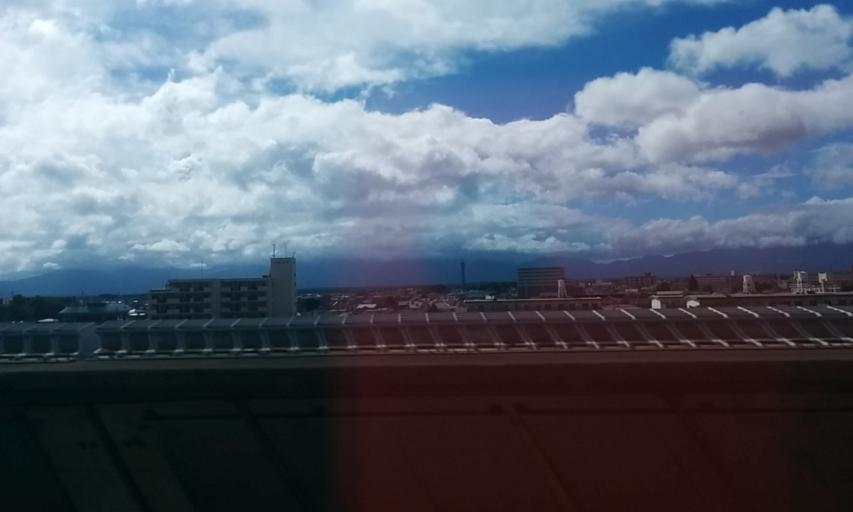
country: JP
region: Tochigi
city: Kuroiso
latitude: 36.9636
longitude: 140.0542
